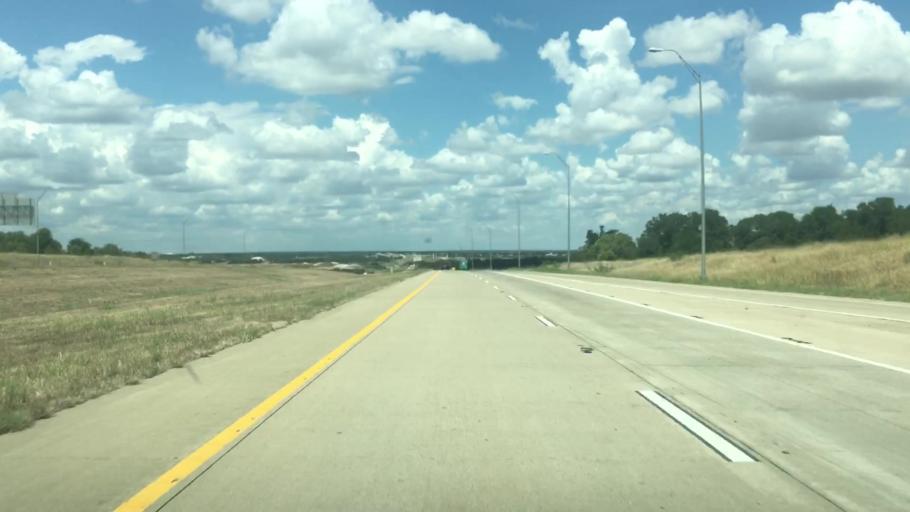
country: US
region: Texas
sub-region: Williamson County
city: Georgetown
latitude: 30.6470
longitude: -97.6322
